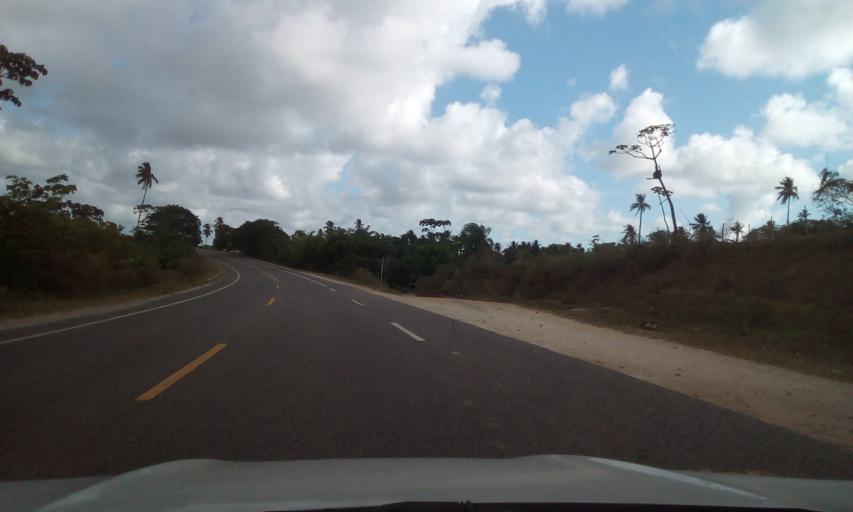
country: BR
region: Bahia
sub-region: Conde
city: Conde
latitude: -11.8002
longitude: -37.6277
